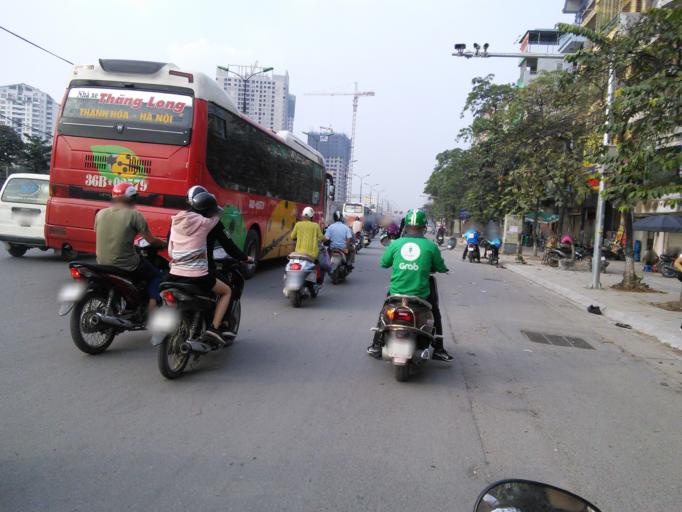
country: VN
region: Ha Noi
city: Hai BaTrung
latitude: 20.9816
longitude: 105.8411
